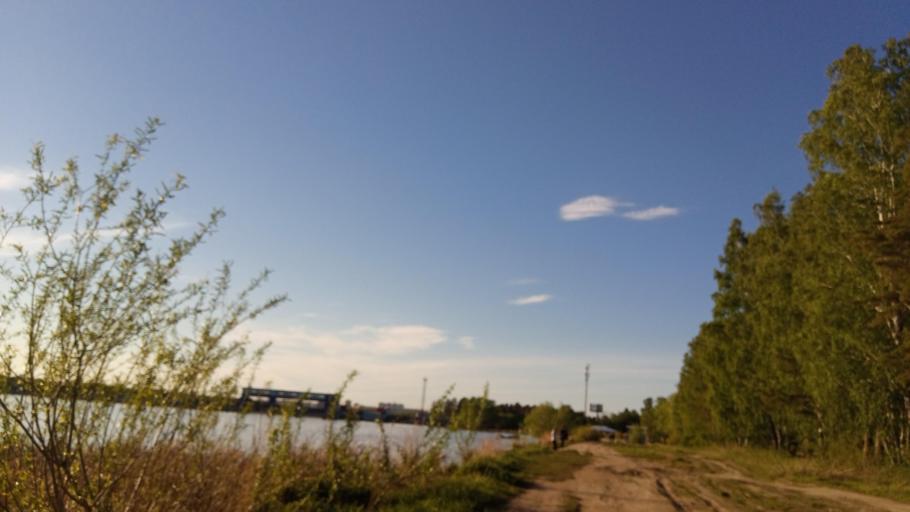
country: RU
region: Chelyabinsk
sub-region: Gorod Chelyabinsk
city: Chelyabinsk
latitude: 55.1428
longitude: 61.3293
